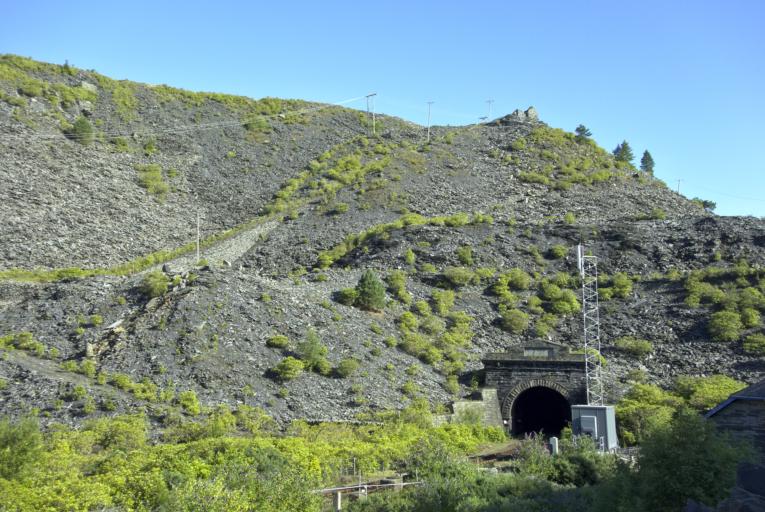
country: GB
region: Wales
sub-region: Gwynedd
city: Blaenau-Ffestiniog
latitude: 53.0028
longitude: -3.9430
